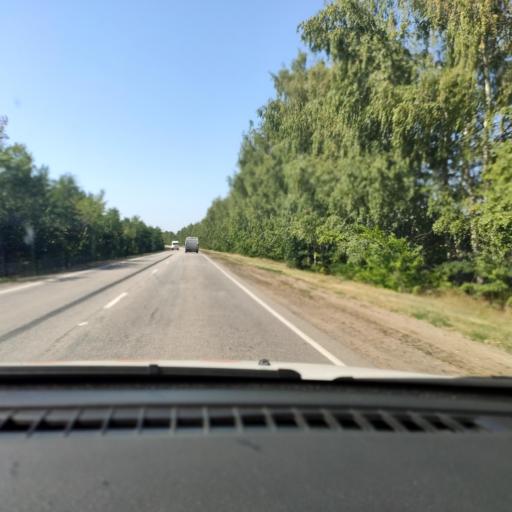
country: RU
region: Voronezj
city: Imeni Pervogo Maya
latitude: 50.7906
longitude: 39.3738
